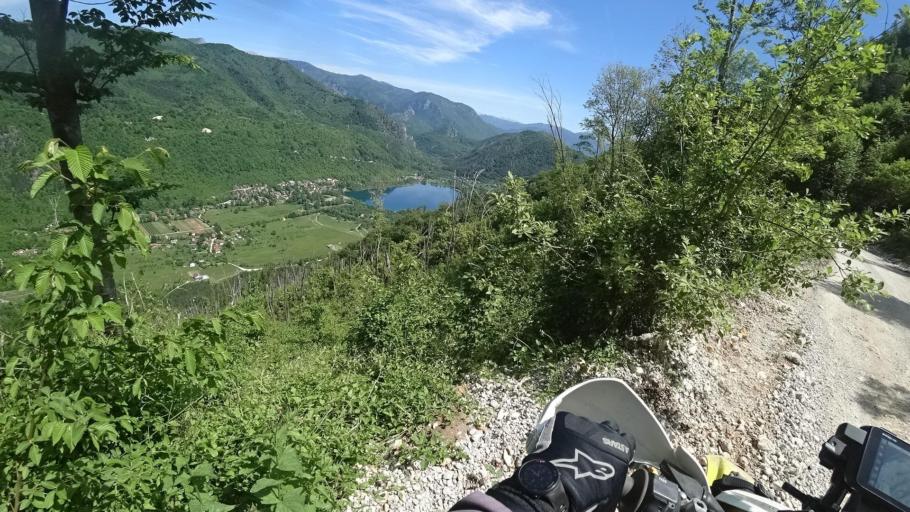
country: BA
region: Federation of Bosnia and Herzegovina
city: Bijela
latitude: 43.5568
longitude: 18.0117
